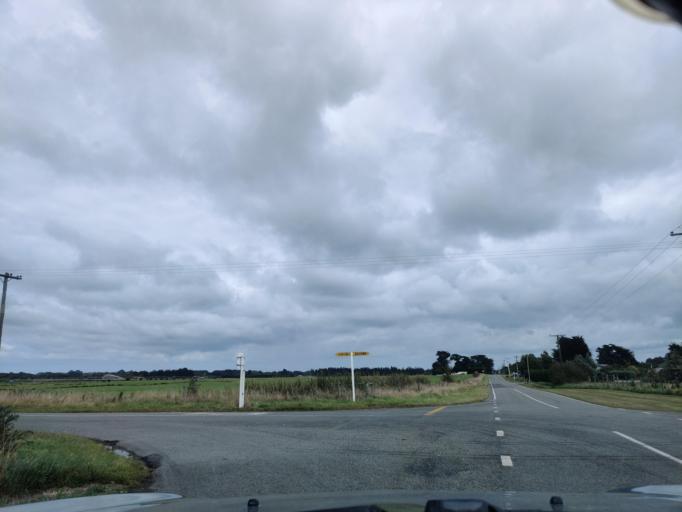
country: NZ
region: Canterbury
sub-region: Hurunui District
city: Amberley
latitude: -43.2384
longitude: 172.6952
